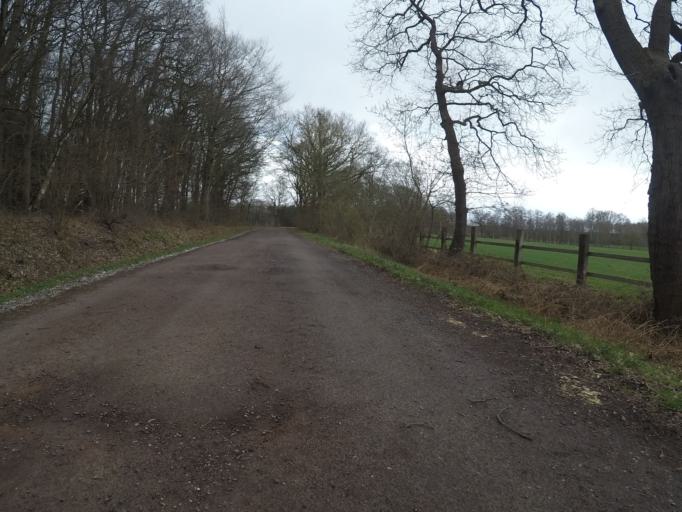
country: DE
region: Lower Saxony
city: Schiffdorf
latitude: 53.6032
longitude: 8.6683
